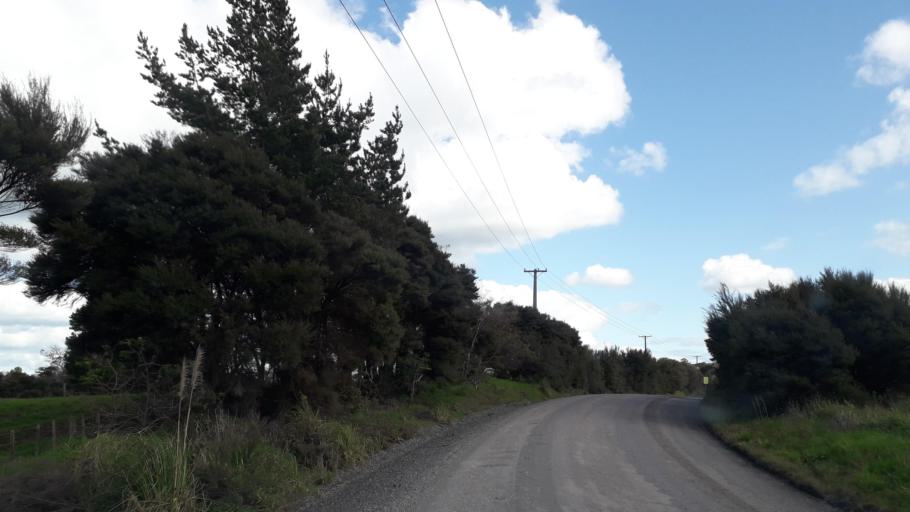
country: NZ
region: Northland
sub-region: Far North District
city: Kerikeri
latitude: -35.1364
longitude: 173.9984
